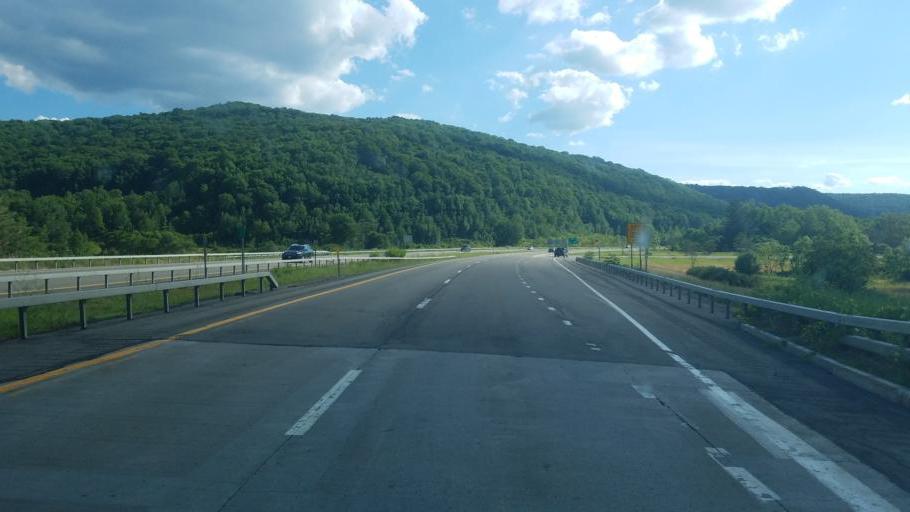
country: US
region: New York
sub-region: Cattaraugus County
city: Salamanca
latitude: 42.1100
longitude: -78.7790
